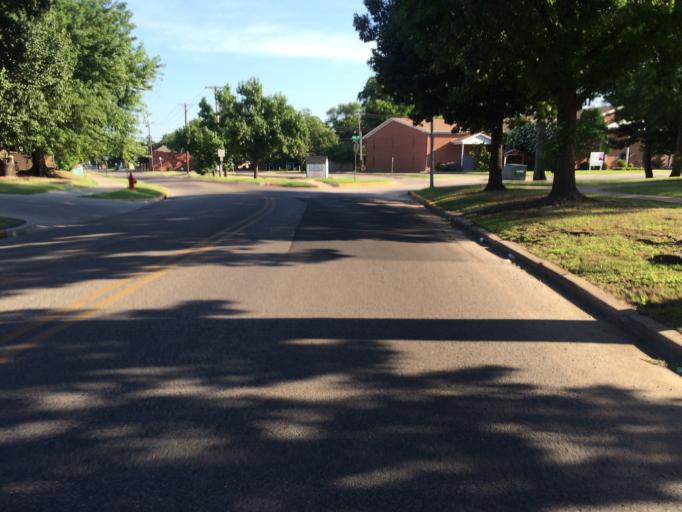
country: US
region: Oklahoma
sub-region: Cleveland County
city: Norman
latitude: 35.2145
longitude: -97.4437
